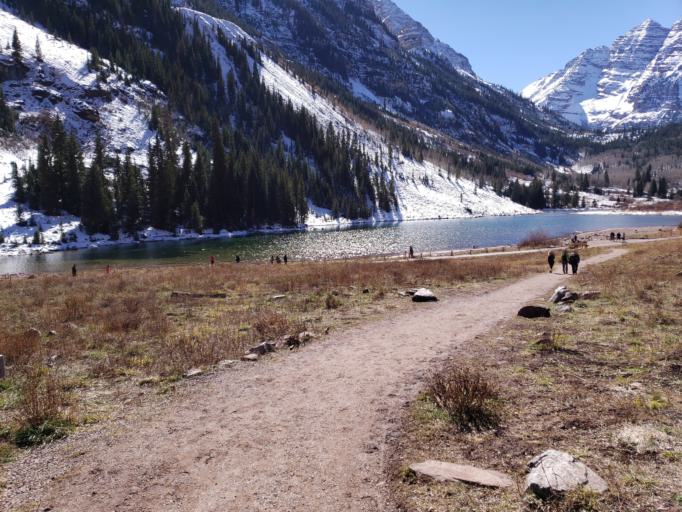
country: US
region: Colorado
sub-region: Pitkin County
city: Snowmass Village
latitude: 39.0988
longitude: -106.9433
